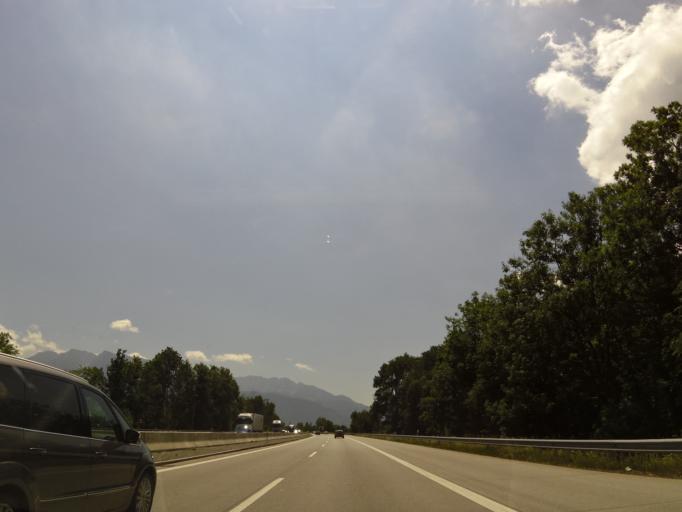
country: AT
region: Tyrol
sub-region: Politischer Bezirk Kufstein
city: Erl
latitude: 47.6846
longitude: 12.1648
